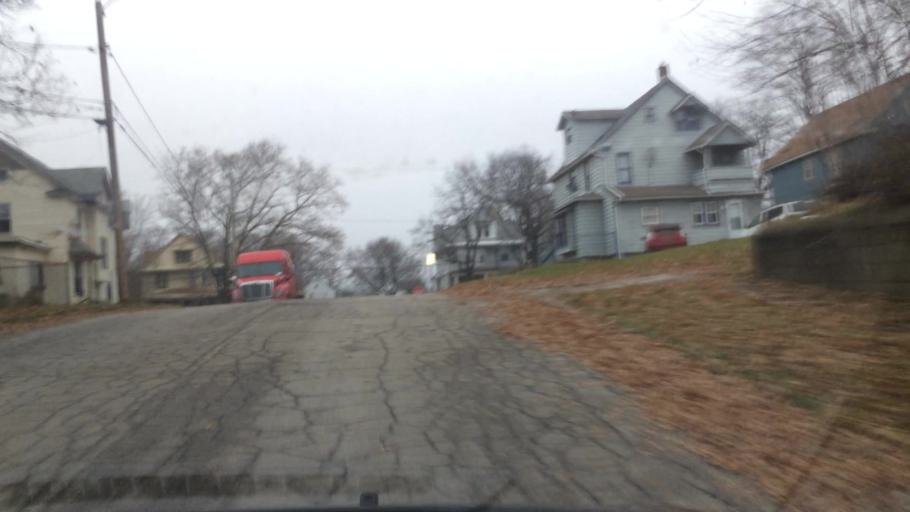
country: US
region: Ohio
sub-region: Summit County
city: Akron
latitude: 41.0569
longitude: -81.5351
